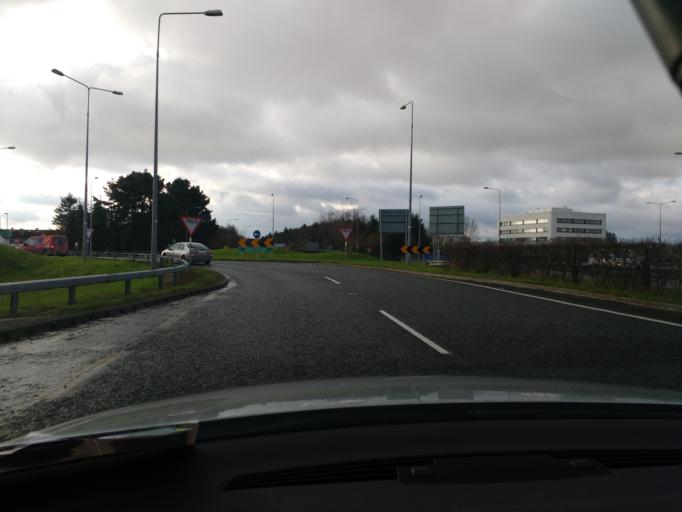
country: IE
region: Munster
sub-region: An Clar
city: Shannon
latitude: 52.7036
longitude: -8.8933
